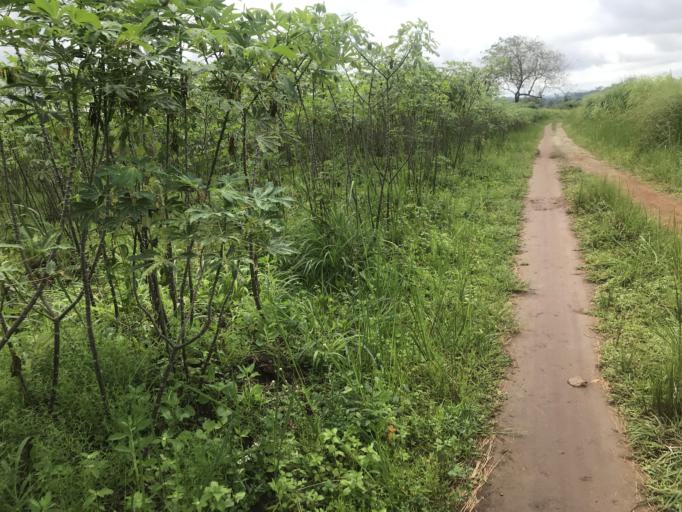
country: SL
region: Eastern Province
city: Buedu
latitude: 8.4648
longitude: -10.3150
